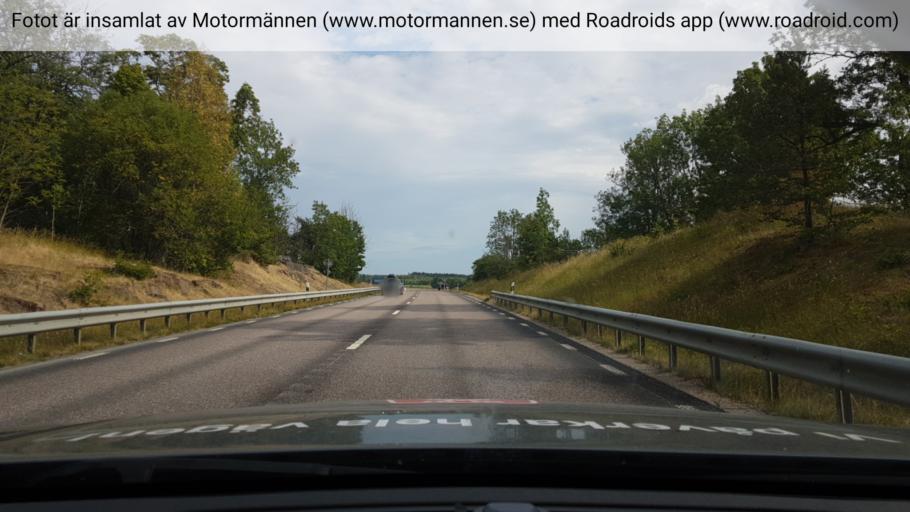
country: SE
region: Uppsala
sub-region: Enkopings Kommun
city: Orsundsbro
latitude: 59.8760
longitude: 17.2897
